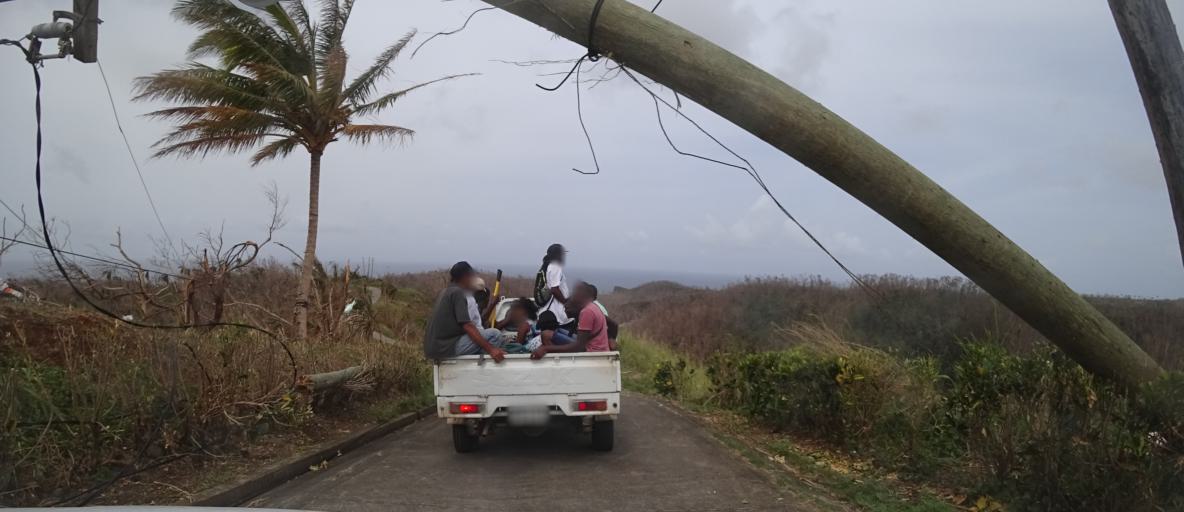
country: DM
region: Saint Andrew
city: Calibishie
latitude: 15.5852
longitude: -61.3721
